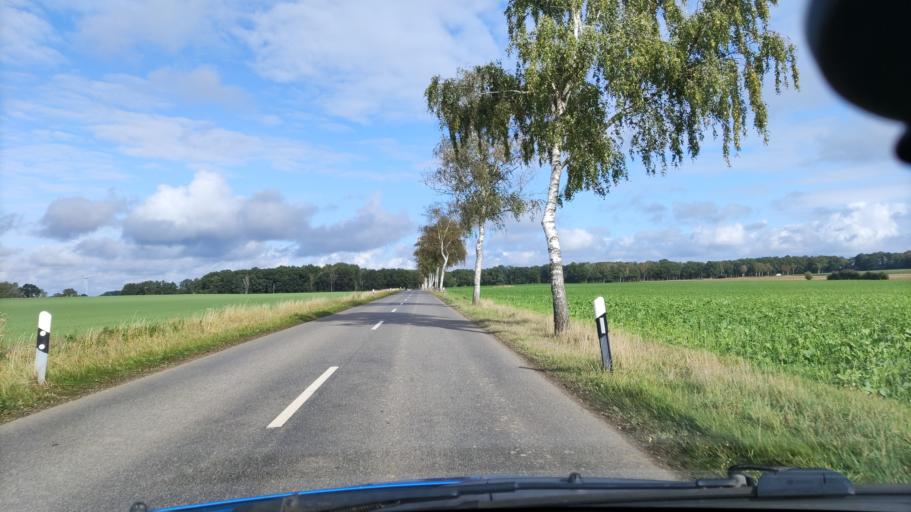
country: DE
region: Lower Saxony
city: Romstedt
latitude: 53.0865
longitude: 10.6729
